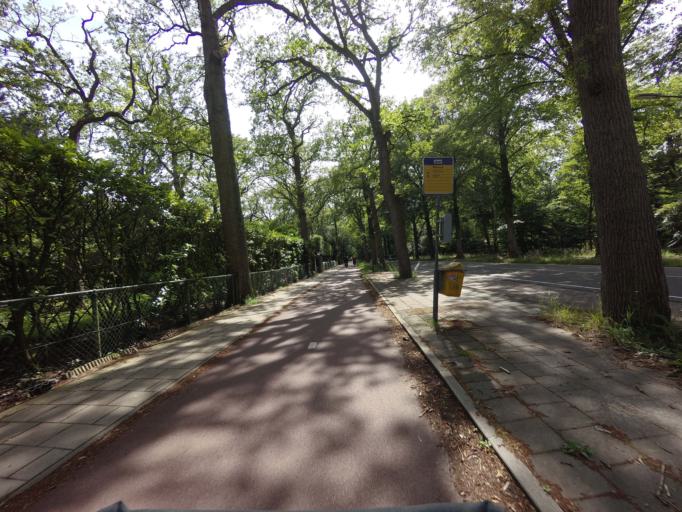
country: NL
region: South Holland
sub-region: Gemeente Wassenaar
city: Wassenaar
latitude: 52.1308
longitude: 4.3747
